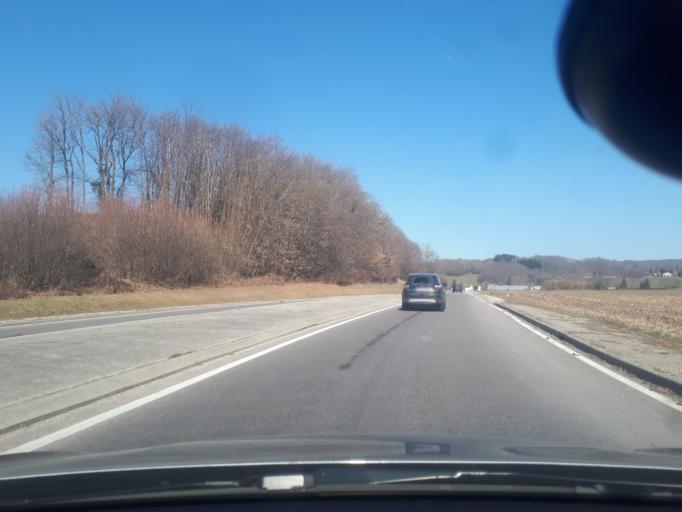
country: FR
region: Rhone-Alpes
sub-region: Departement de l'Isere
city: Champier
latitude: 45.4379
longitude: 5.2866
